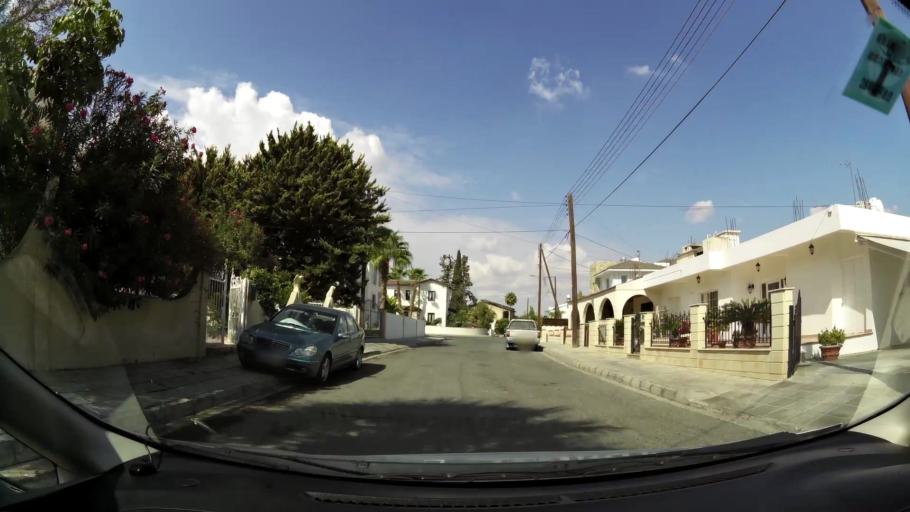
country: CY
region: Larnaka
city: Aradippou
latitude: 34.9431
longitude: 33.5910
